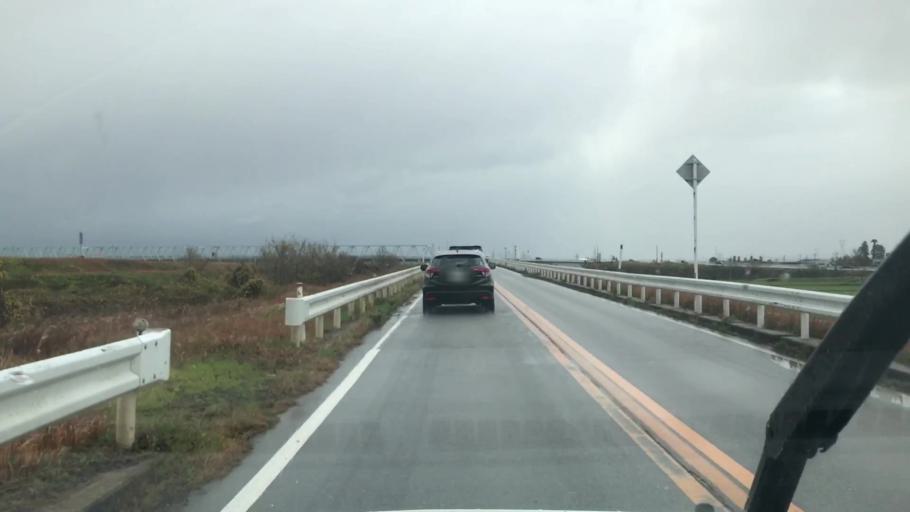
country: JP
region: Toyama
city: Toyama-shi
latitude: 36.6687
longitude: 137.2869
